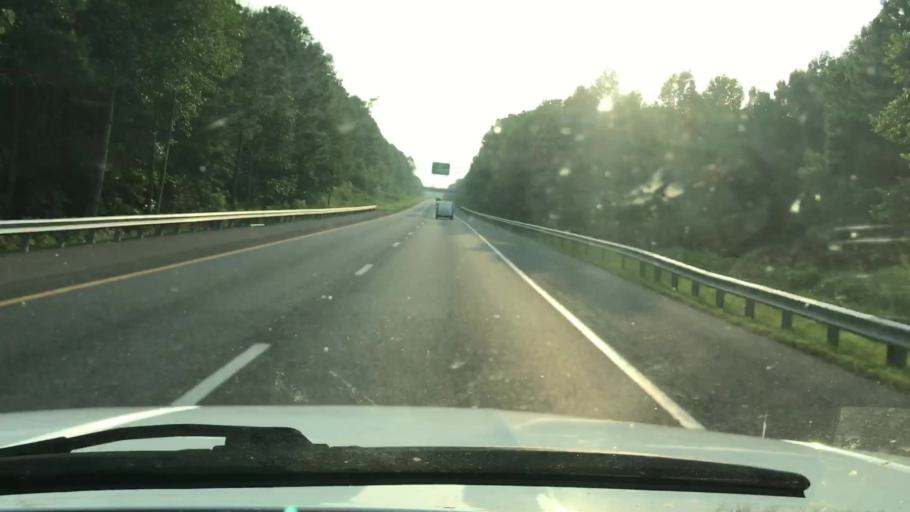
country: US
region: Virginia
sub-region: Chesterfield County
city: Brandermill
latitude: 37.4109
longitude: -77.5977
